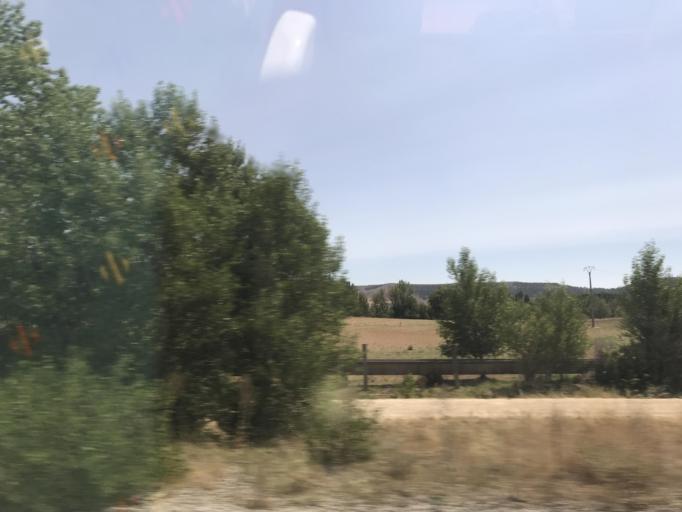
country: ES
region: Castille and Leon
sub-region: Provincia de Valladolid
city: Cubillas de Santa Marta
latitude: 41.8018
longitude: -4.5843
